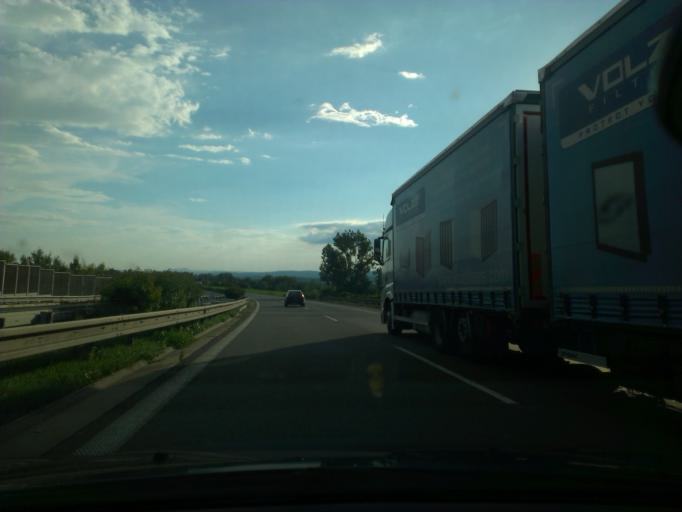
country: SK
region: Nitriansky
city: Ilava
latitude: 49.0456
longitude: 18.2844
